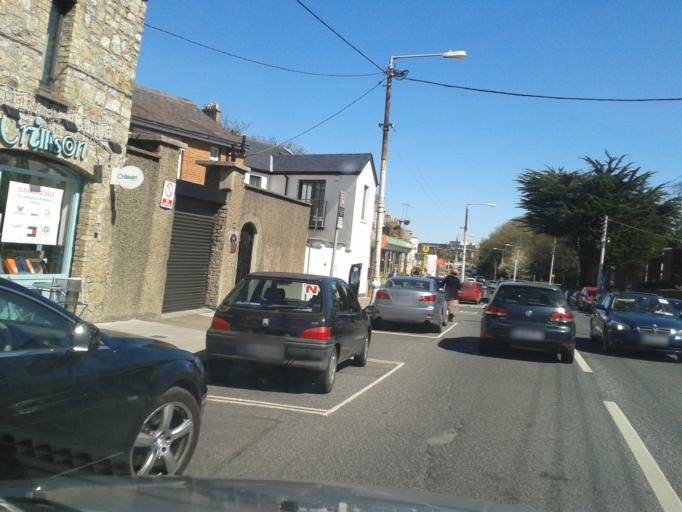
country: IE
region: Leinster
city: Monkstown
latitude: 53.2939
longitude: -6.1501
